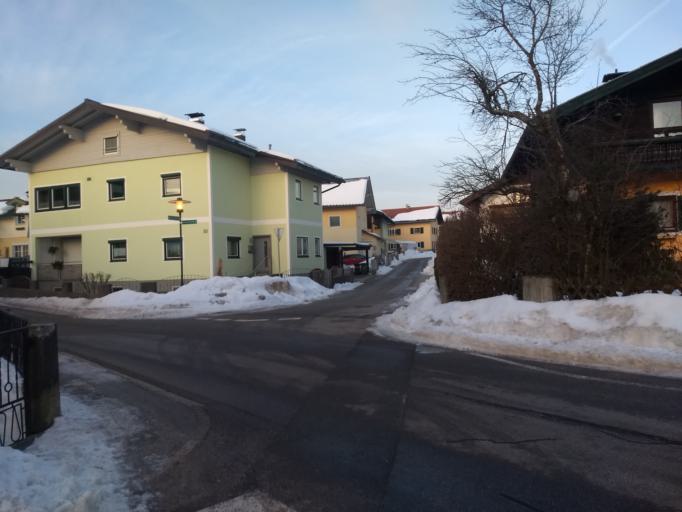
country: AT
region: Salzburg
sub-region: Politischer Bezirk Salzburg-Umgebung
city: Seekirchen am Wallersee
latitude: 47.8906
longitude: 13.1227
